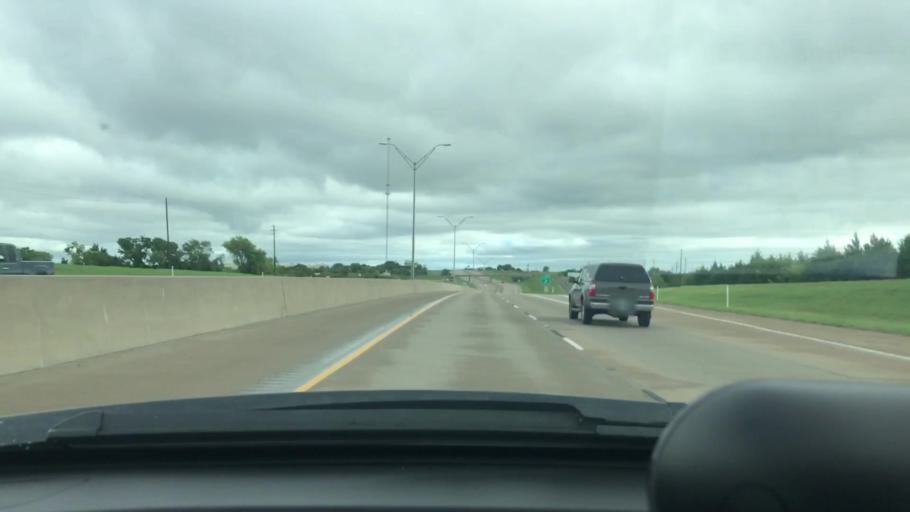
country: US
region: Texas
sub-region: Grayson County
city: Howe
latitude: 33.5232
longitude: -96.6142
